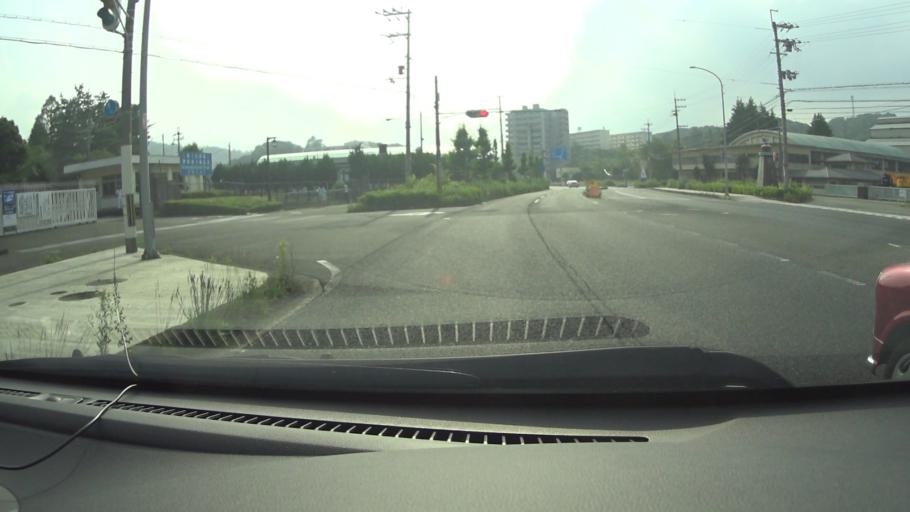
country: JP
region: Kyoto
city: Maizuru
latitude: 35.4763
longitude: 135.3720
